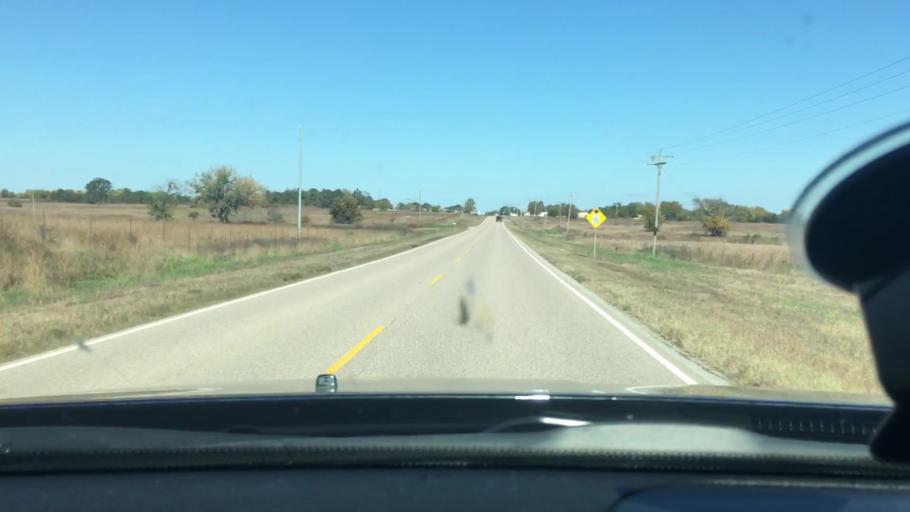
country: US
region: Oklahoma
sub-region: Johnston County
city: Tishomingo
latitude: 34.4357
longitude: -96.6359
